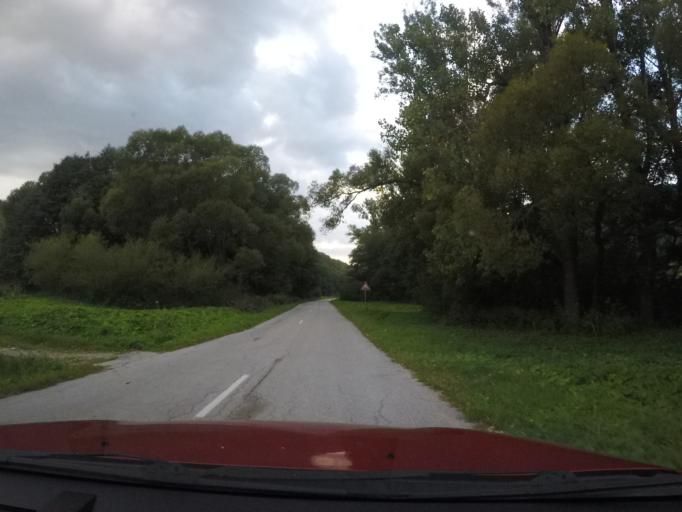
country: SK
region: Kosicky
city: Medzev
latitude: 48.6285
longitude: 20.7402
